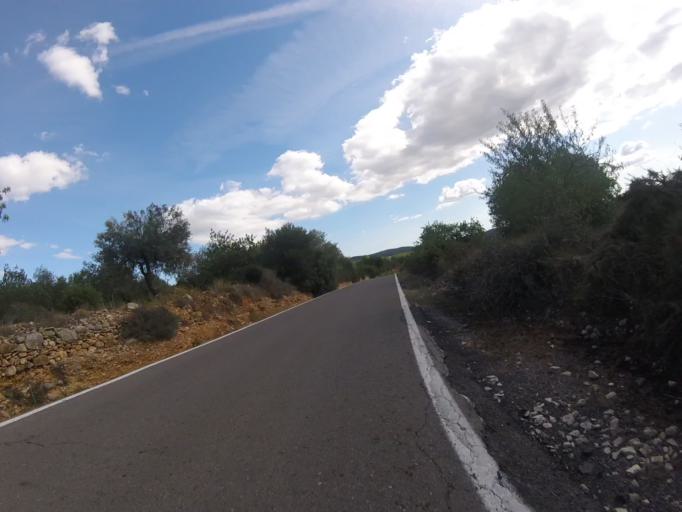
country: ES
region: Valencia
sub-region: Provincia de Castello
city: Cuevas de Vinroma
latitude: 40.3736
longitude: 0.1144
